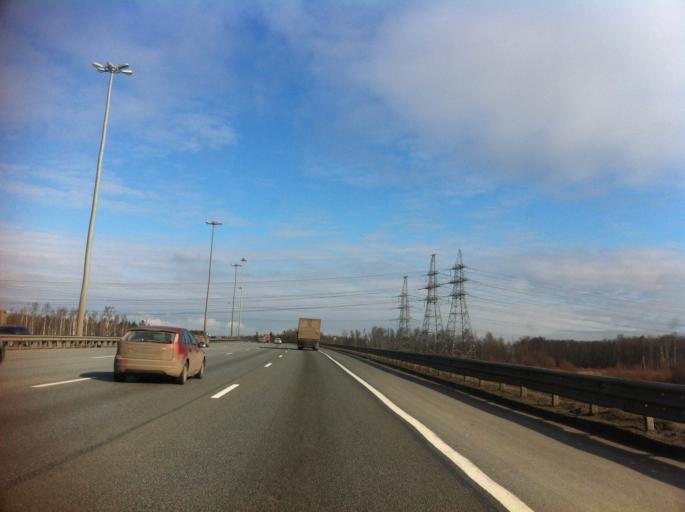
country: RU
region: St.-Petersburg
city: Krasnogvargeisky
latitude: 59.9274
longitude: 30.5336
